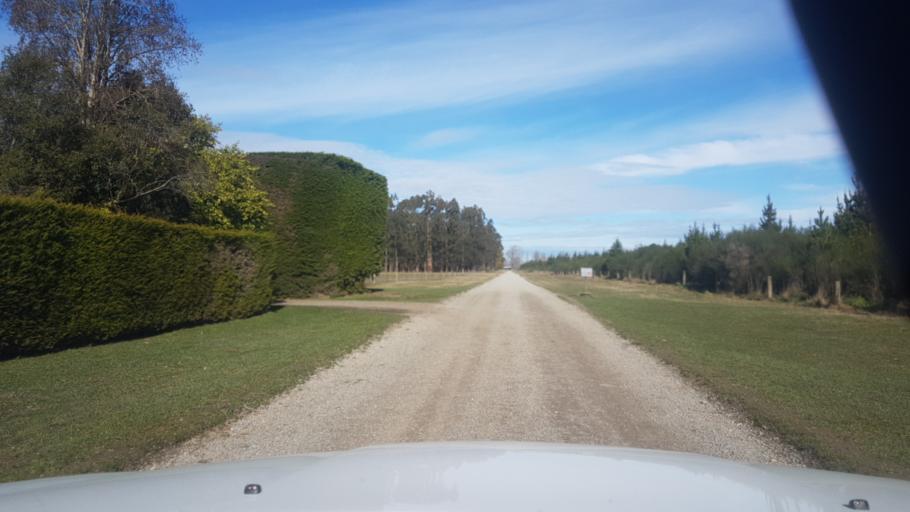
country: NZ
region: Canterbury
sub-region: Timaru District
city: Pleasant Point
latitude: -44.1376
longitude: 171.2768
